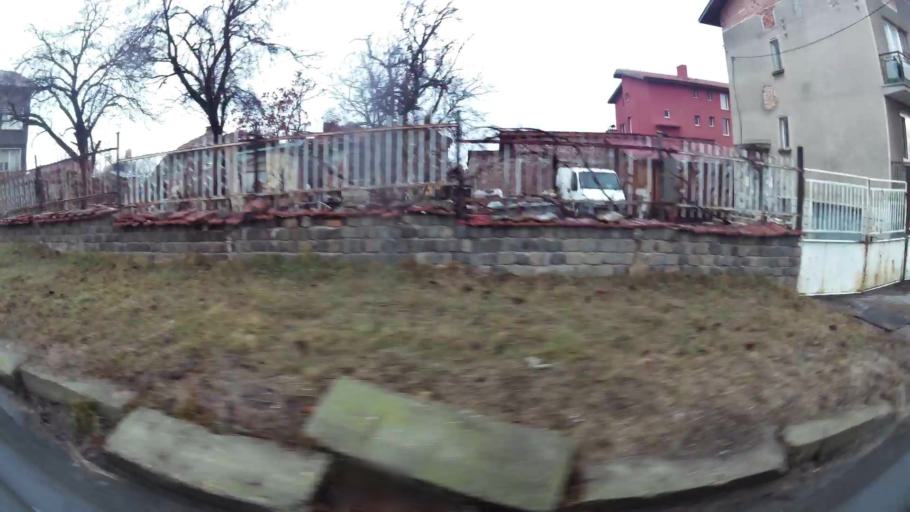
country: BG
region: Sofia-Capital
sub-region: Stolichna Obshtina
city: Sofia
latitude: 42.7466
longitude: 23.3497
